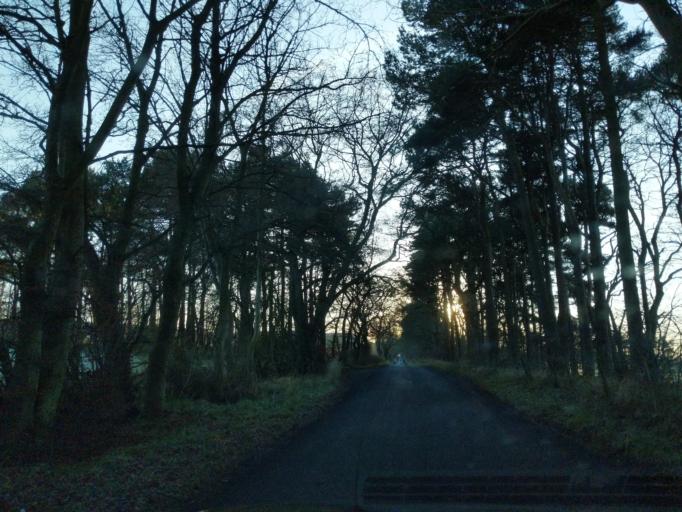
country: GB
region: Scotland
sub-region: Edinburgh
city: Balerno
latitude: 55.8748
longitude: -3.3566
